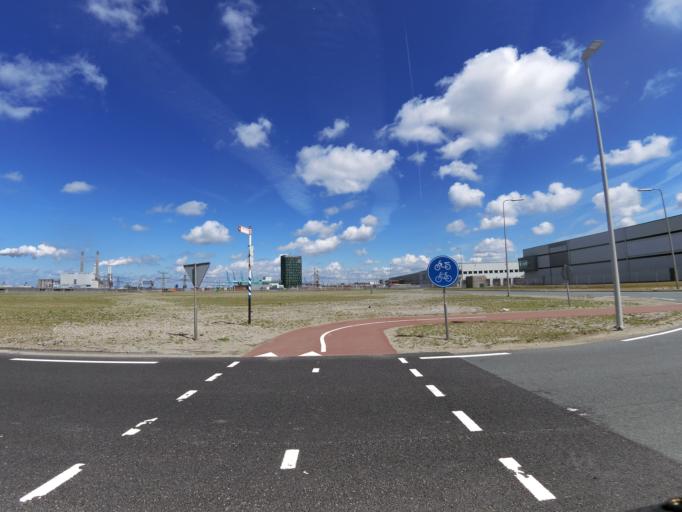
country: NL
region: South Holland
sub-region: Gemeente Rotterdam
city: Hoek van Holland
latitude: 51.9455
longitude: 4.0128
